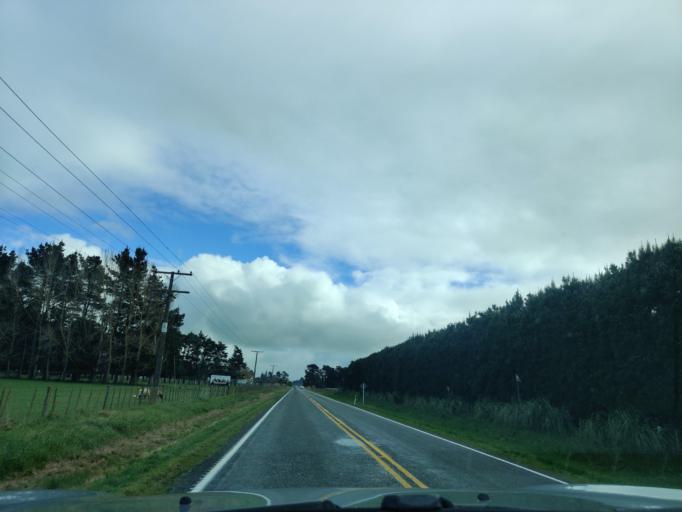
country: NZ
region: Hawke's Bay
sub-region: Hastings District
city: Hastings
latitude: -40.0165
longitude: 176.3553
